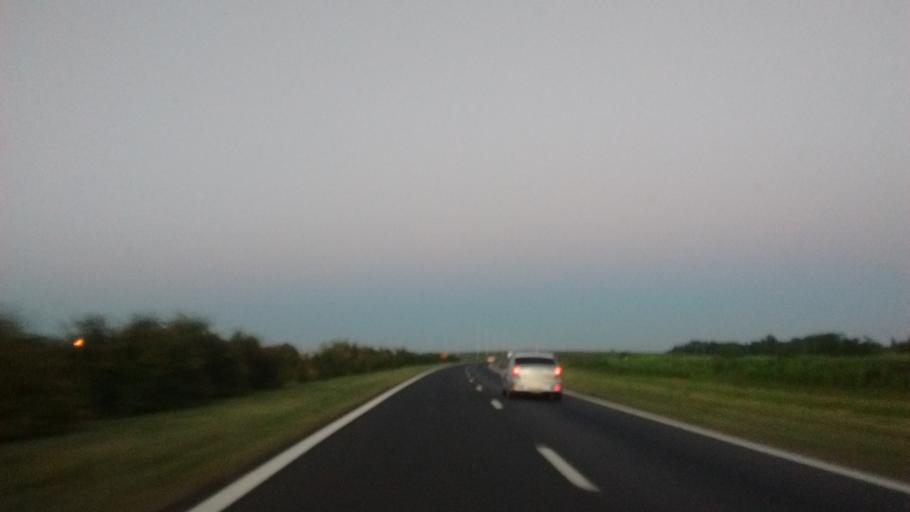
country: AR
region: Santa Fe
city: Roldan
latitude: -32.9277
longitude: -60.8920
